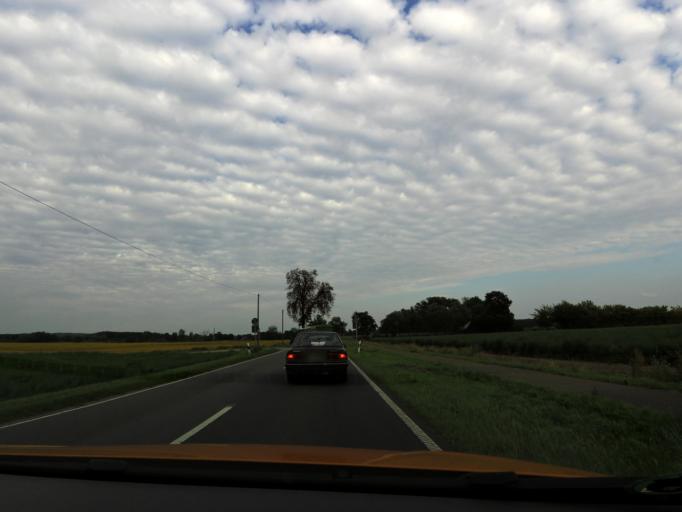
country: DE
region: Brandenburg
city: Roskow
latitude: 52.4084
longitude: 12.6759
